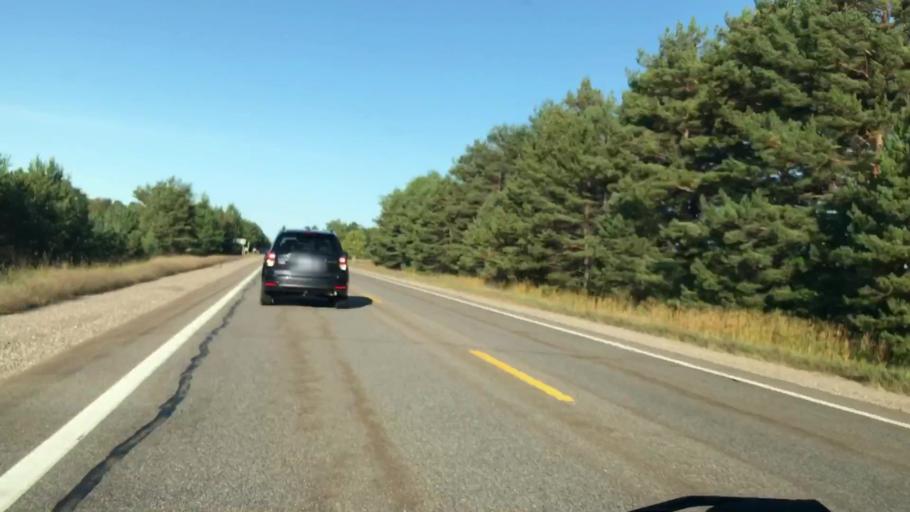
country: US
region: Michigan
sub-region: Chippewa County
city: Sault Ste. Marie
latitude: 46.3756
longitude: -84.6143
